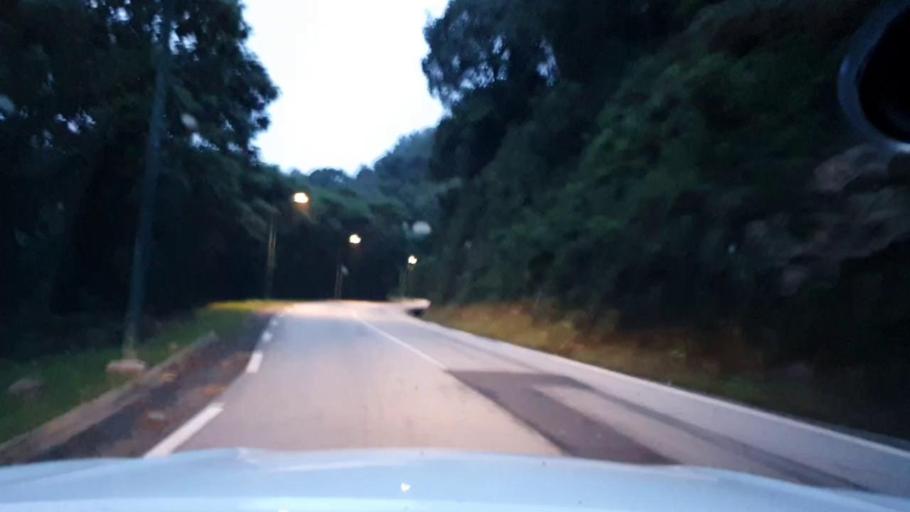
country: RW
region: Southern Province
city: Nzega
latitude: -2.5282
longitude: 29.3758
